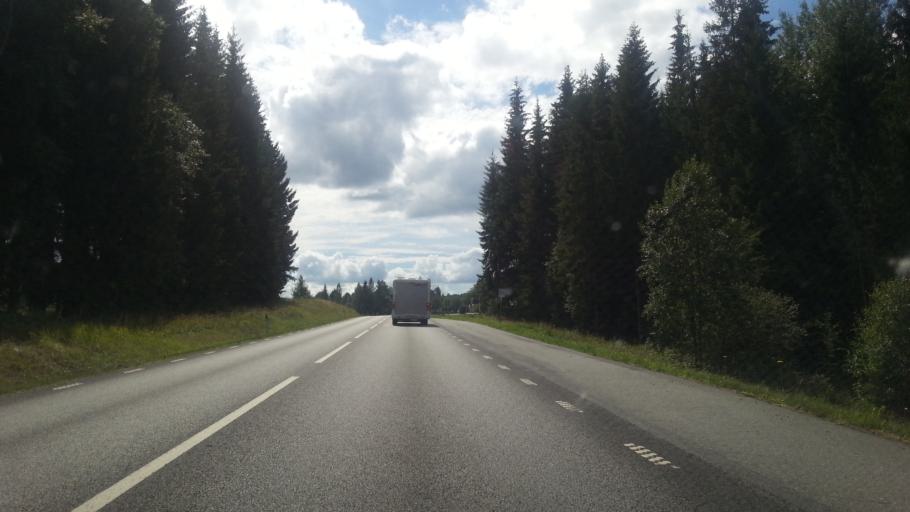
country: SE
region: OErebro
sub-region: Lindesbergs Kommun
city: Stora
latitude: 59.6746
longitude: 15.1001
